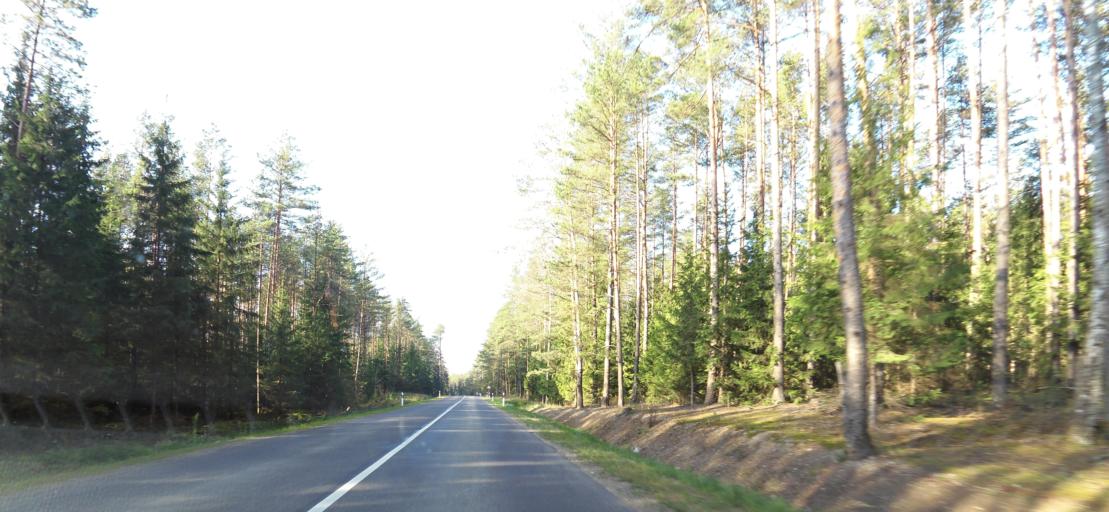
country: LT
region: Vilnius County
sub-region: Trakai
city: Rudiskes
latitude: 54.5097
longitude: 24.8932
